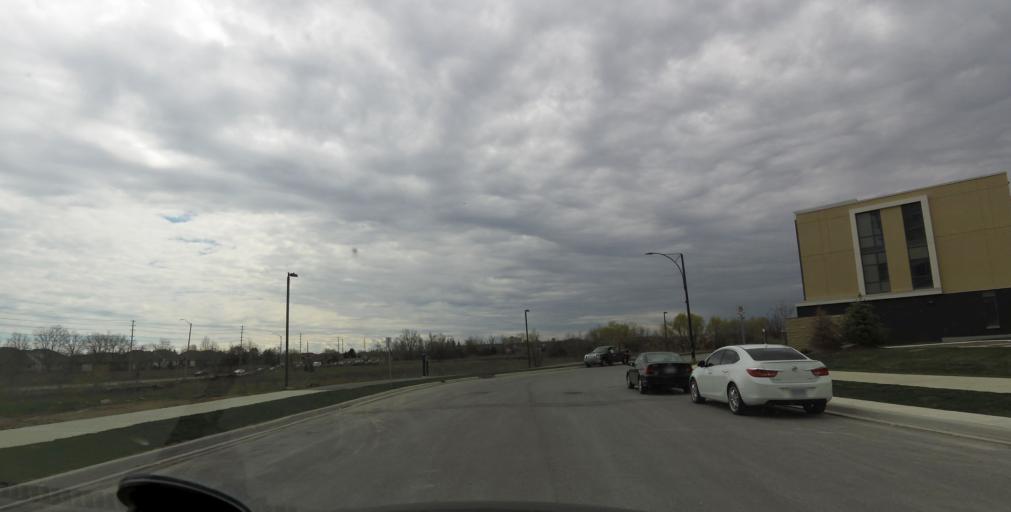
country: CA
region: Ontario
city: Mississauga
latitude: 43.6058
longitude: -79.6555
